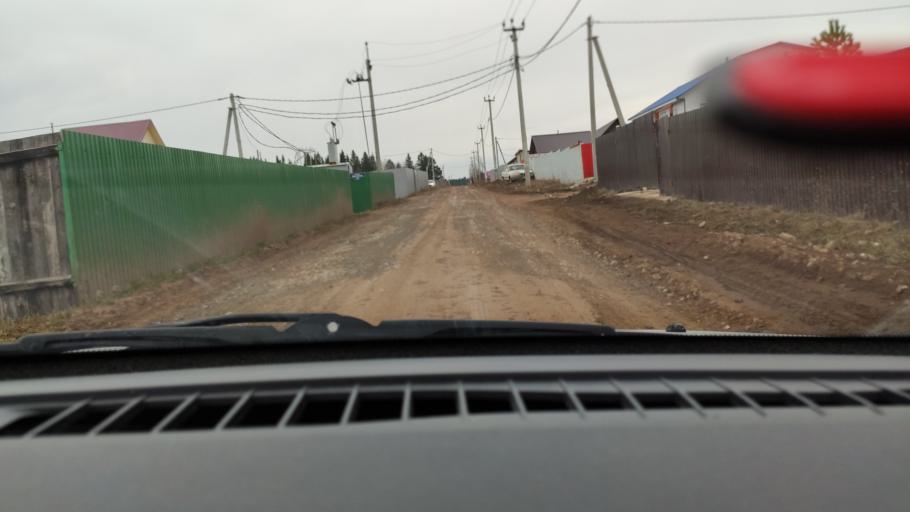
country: RU
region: Perm
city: Kultayevo
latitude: 57.8985
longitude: 56.0050
